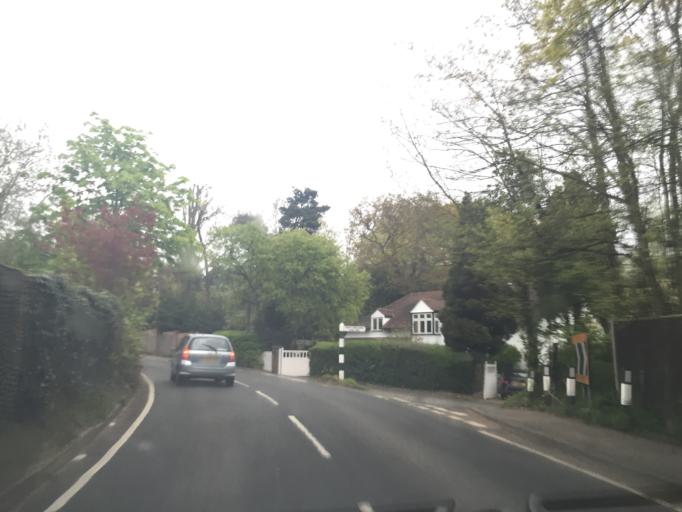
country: GB
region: England
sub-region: Essex
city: Theydon Bois
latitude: 51.6870
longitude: 0.0967
